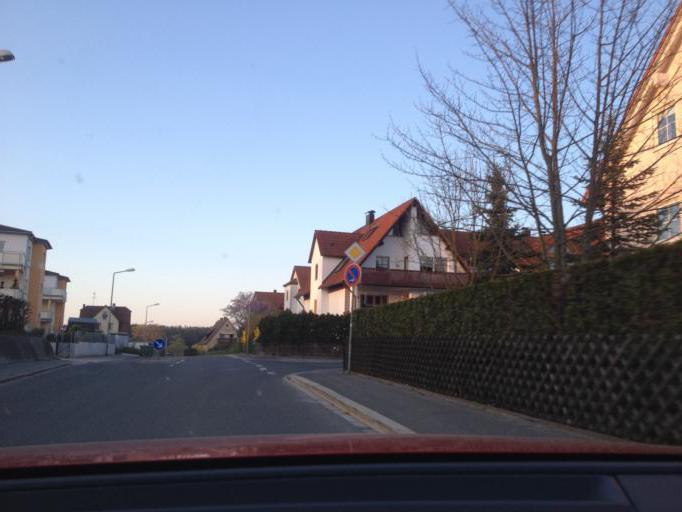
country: DE
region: Bavaria
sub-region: Regierungsbezirk Mittelfranken
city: Lauf an der Pegnitz
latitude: 49.5203
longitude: 11.2813
